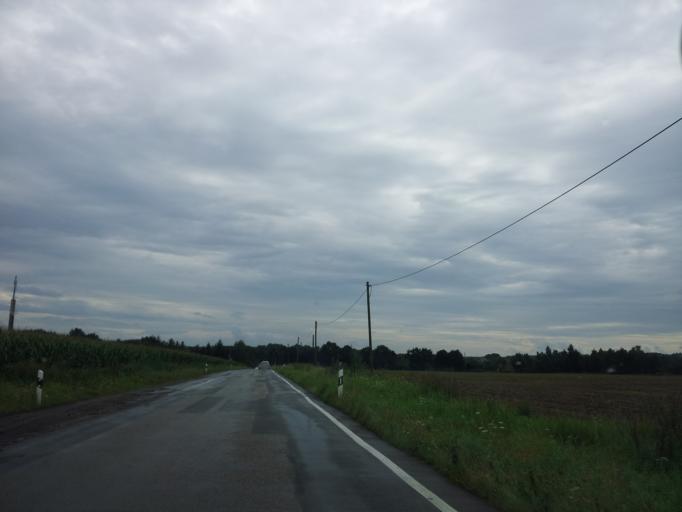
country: DE
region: Brandenburg
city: Gorzke
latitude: 52.1795
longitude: 12.3799
